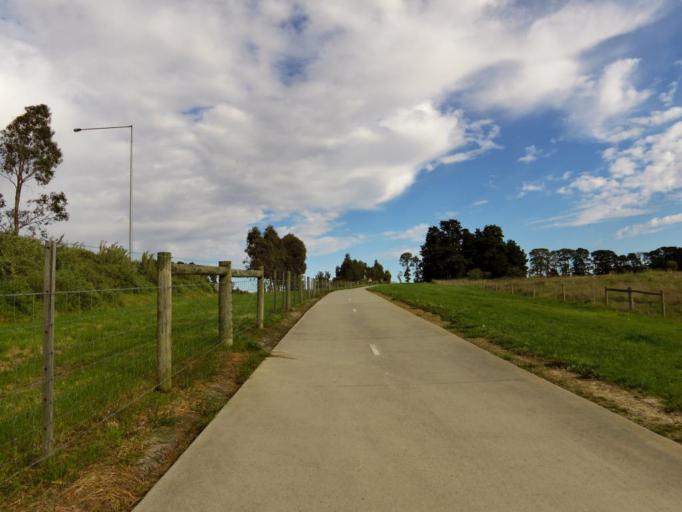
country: AU
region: Victoria
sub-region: Knox
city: Wantirna
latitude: -37.8634
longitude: 145.2108
